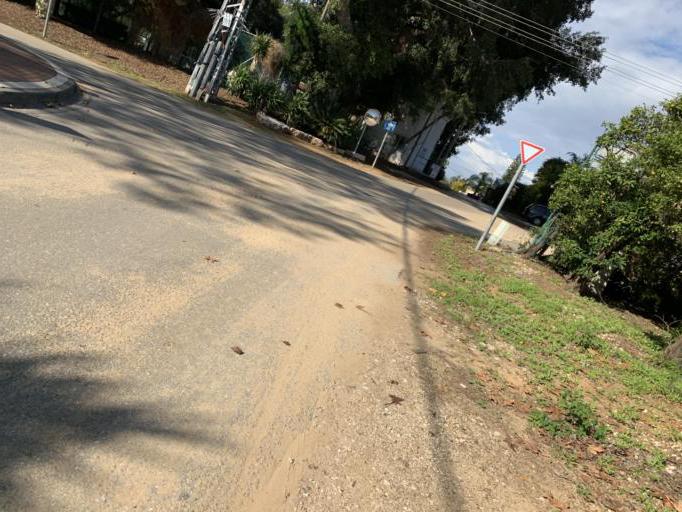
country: IL
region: Central District
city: Ra'anana
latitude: 32.1671
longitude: 34.8764
